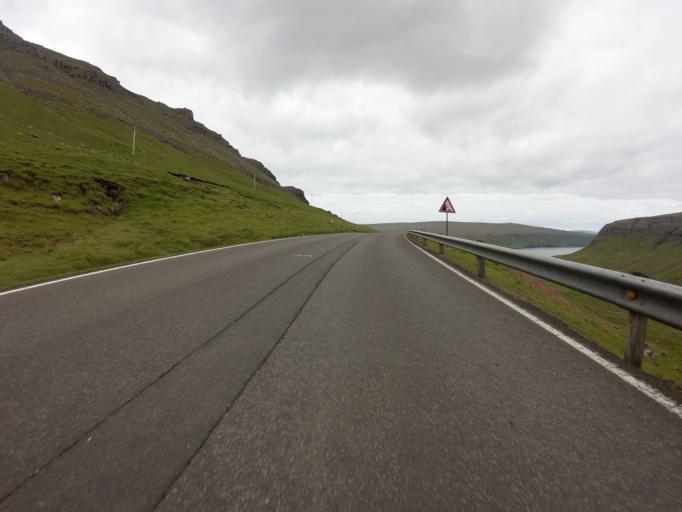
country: FO
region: Suduroy
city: Tvoroyri
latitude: 61.5743
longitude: -6.9368
